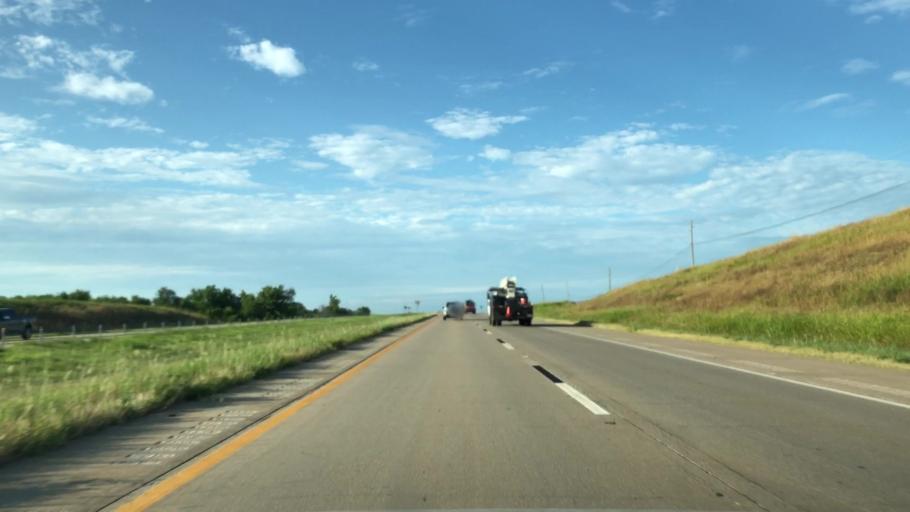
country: US
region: Oklahoma
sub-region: Osage County
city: Skiatook
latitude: 36.4837
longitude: -95.9207
